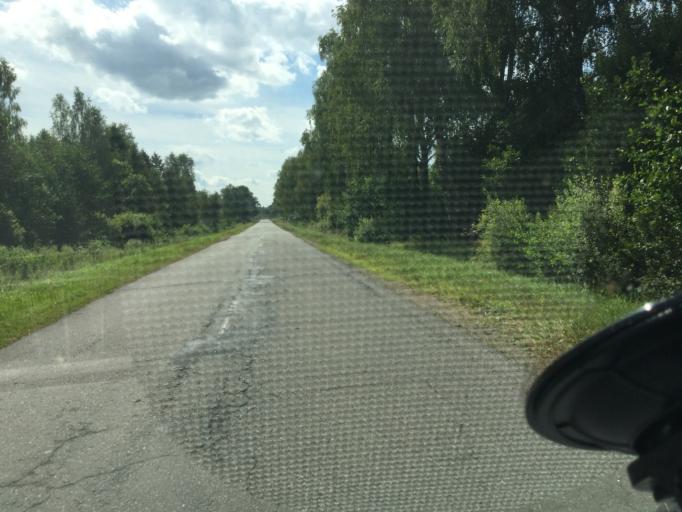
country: BY
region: Vitebsk
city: Chashniki
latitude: 55.2929
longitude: 29.3683
